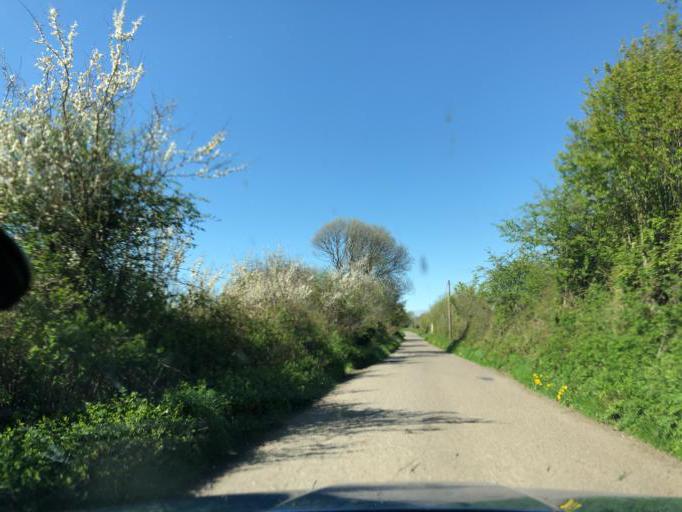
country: IE
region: Connaught
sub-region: County Galway
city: Portumna
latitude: 53.1574
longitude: -8.3267
